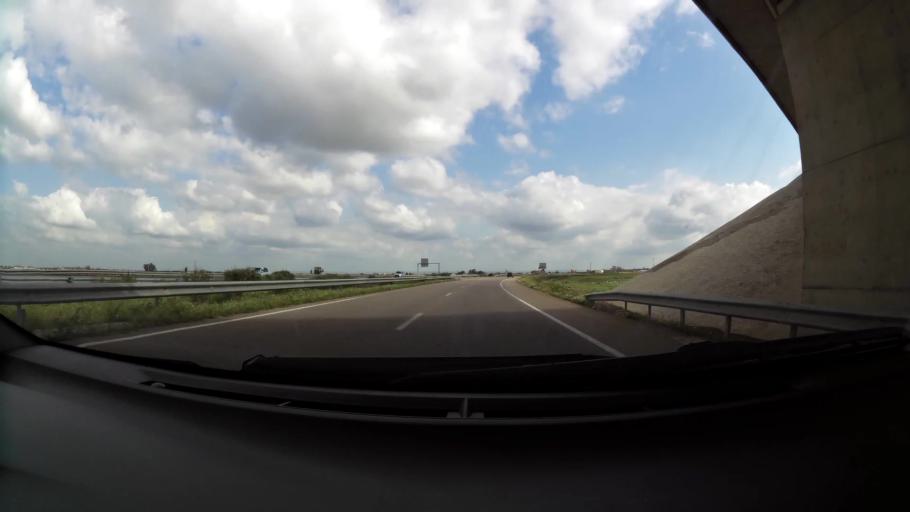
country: MA
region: Chaouia-Ouardigha
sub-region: Settat Province
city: Berrechid
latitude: 33.2884
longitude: -7.5479
